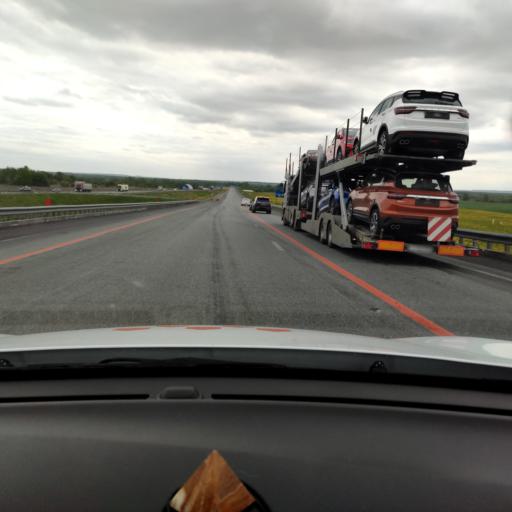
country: RU
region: Tatarstan
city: Pestretsy
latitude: 55.7057
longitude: 49.5643
